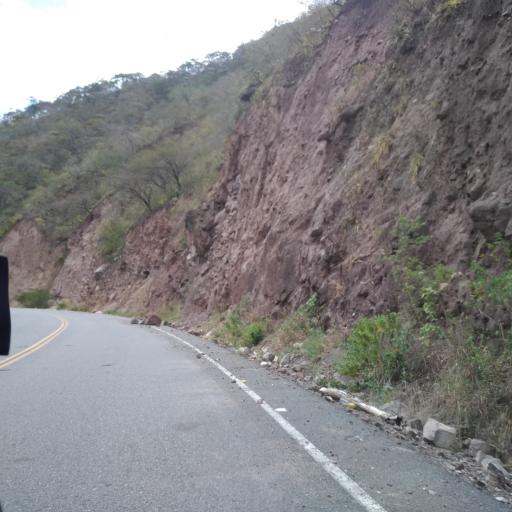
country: PE
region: Cajamarca
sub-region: Provincia de San Ignacio
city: Chirinos
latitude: -5.2439
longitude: -78.8428
